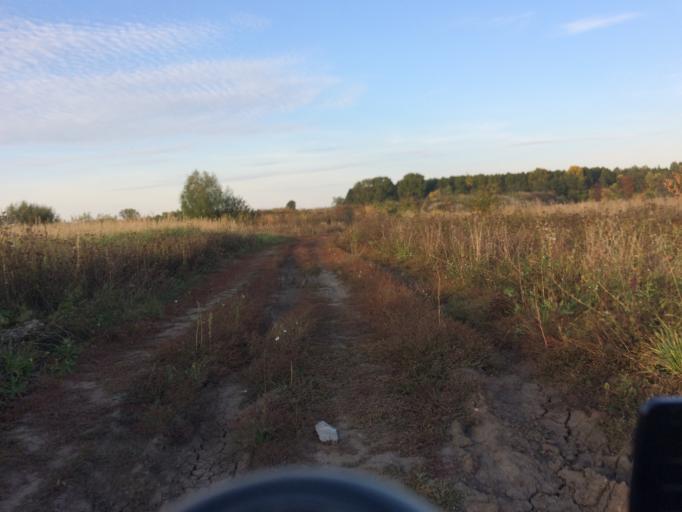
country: RU
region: Mariy-El
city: Yoshkar-Ola
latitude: 56.6471
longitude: 47.9223
